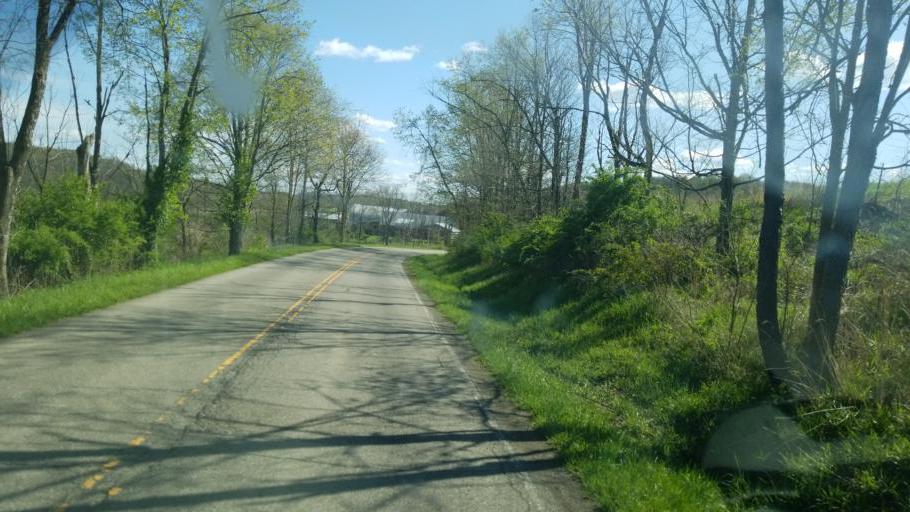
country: US
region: Ohio
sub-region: Coshocton County
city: Coshocton
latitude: 40.3874
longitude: -81.8490
